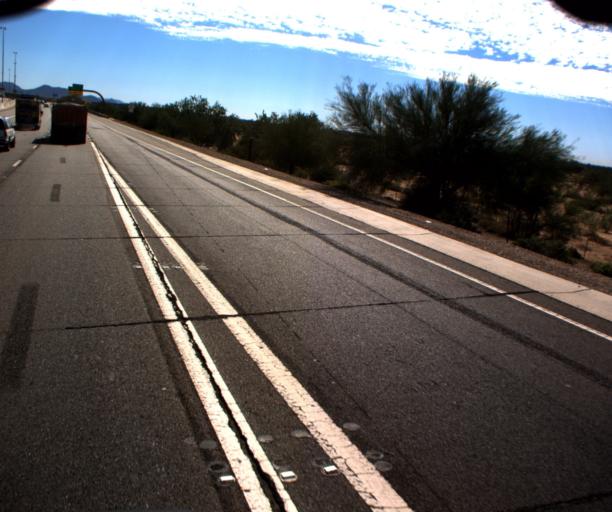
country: US
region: Arizona
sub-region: Maricopa County
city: Paradise Valley
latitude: 33.6654
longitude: -111.9550
